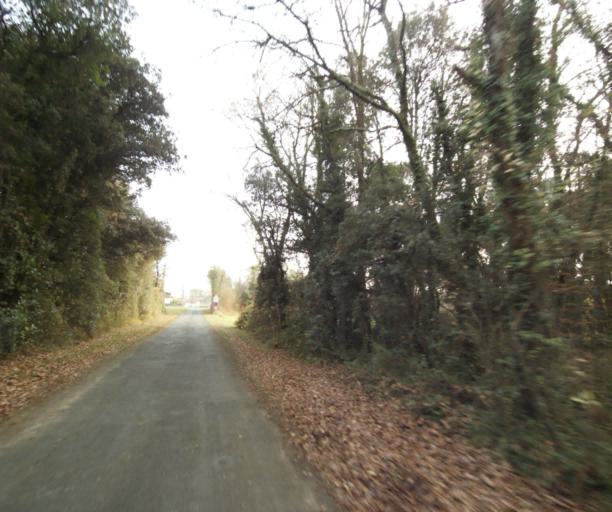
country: FR
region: Poitou-Charentes
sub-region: Departement de la Charente-Maritime
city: Saint-Hilaire-de-Villefranche
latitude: 45.8172
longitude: -0.5637
